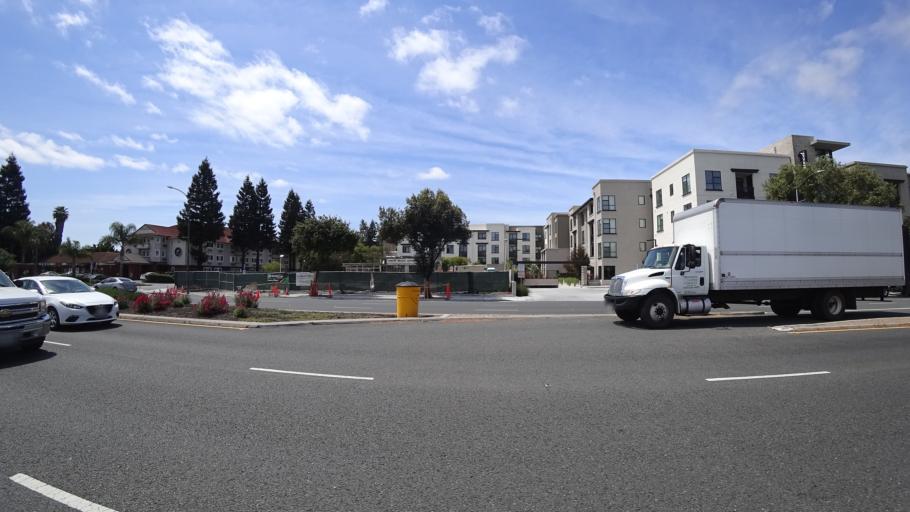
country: US
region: California
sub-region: Santa Clara County
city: Sunnyvale
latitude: 37.3752
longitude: -122.0595
